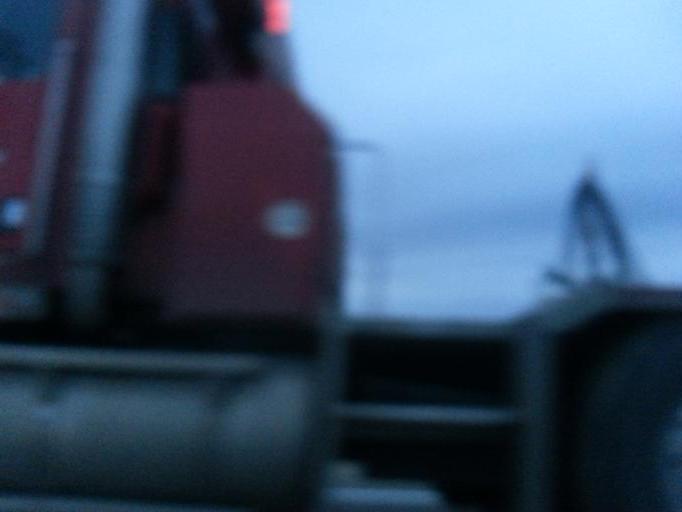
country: US
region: Iowa
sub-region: Black Hawk County
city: La Porte City
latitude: 42.4089
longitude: -92.1654
